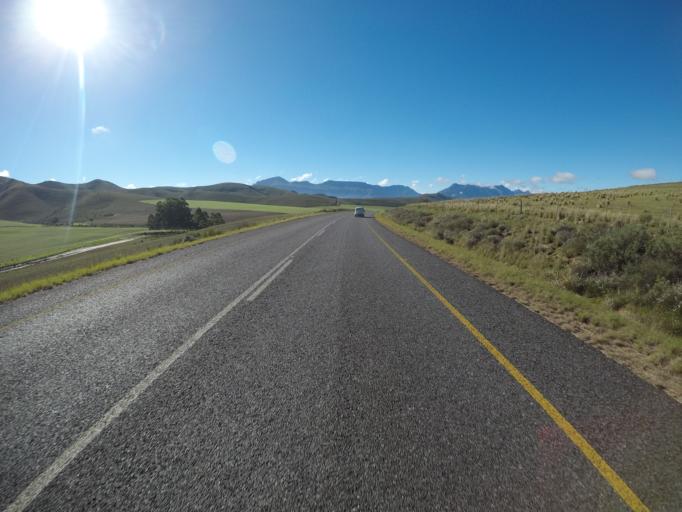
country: ZA
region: Western Cape
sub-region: Overberg District Municipality
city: Caledon
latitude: -34.0998
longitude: 19.5291
